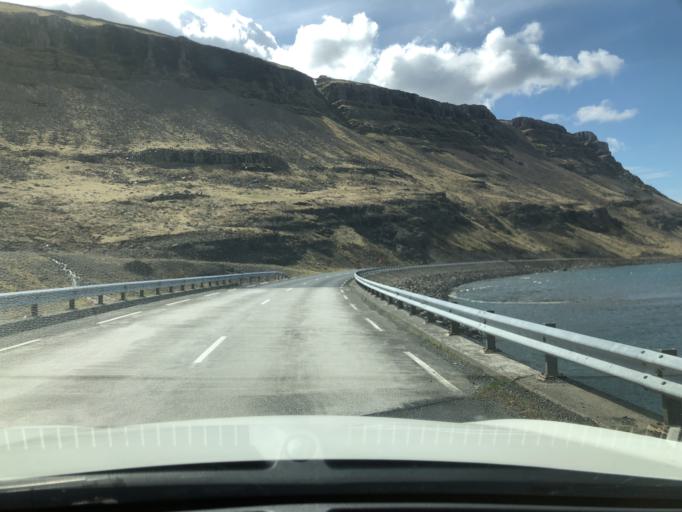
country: IS
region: Capital Region
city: Mosfellsbaer
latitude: 64.3827
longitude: -21.3553
